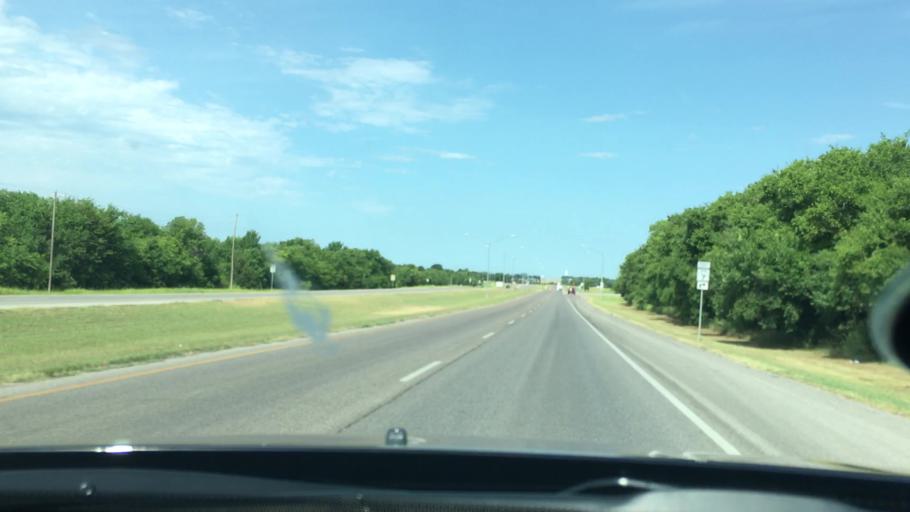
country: US
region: Oklahoma
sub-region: Murray County
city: Sulphur
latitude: 34.5064
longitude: -97.0087
